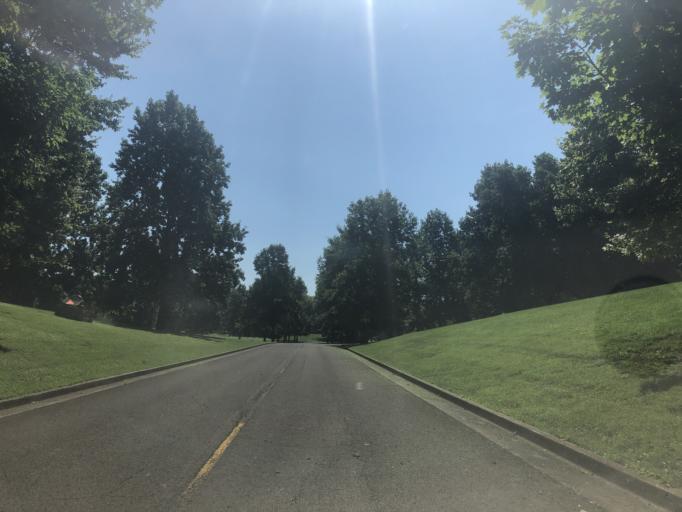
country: US
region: Tennessee
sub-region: Davidson County
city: Lakewood
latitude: 36.2126
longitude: -86.6068
